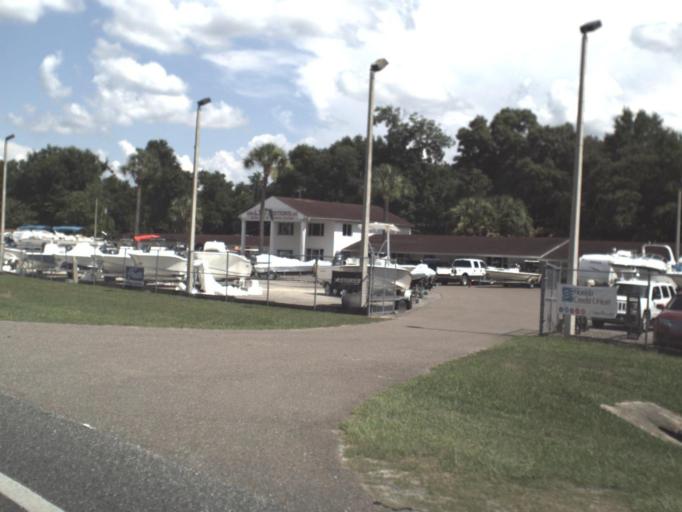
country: US
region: Florida
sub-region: Alachua County
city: High Springs
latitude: 29.8116
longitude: -82.5618
